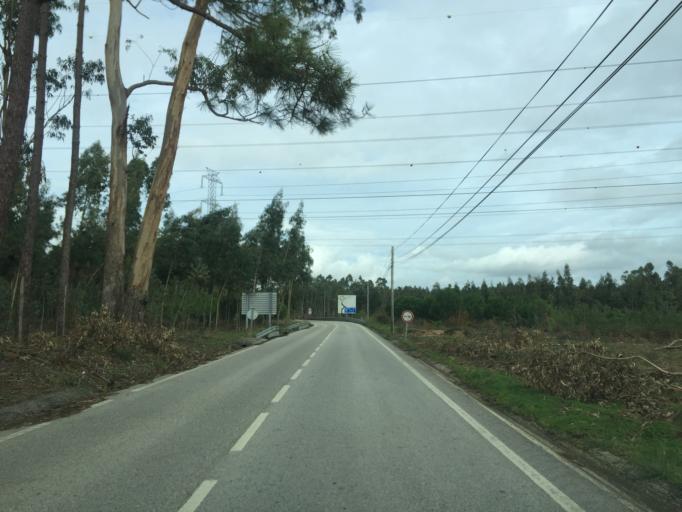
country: PT
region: Coimbra
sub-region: Figueira da Foz
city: Lavos
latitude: 40.0464
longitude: -8.8170
